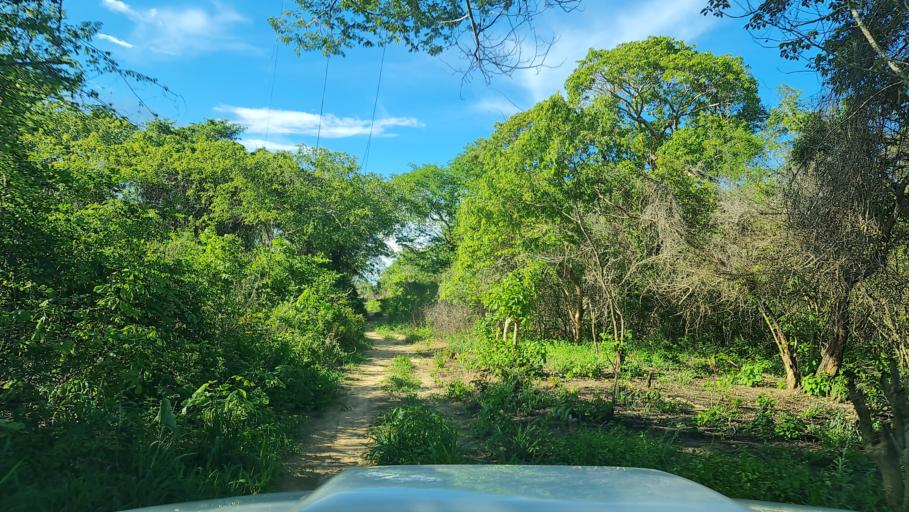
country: MZ
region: Nampula
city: Ilha de Mocambique
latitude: -15.2617
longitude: 40.1851
